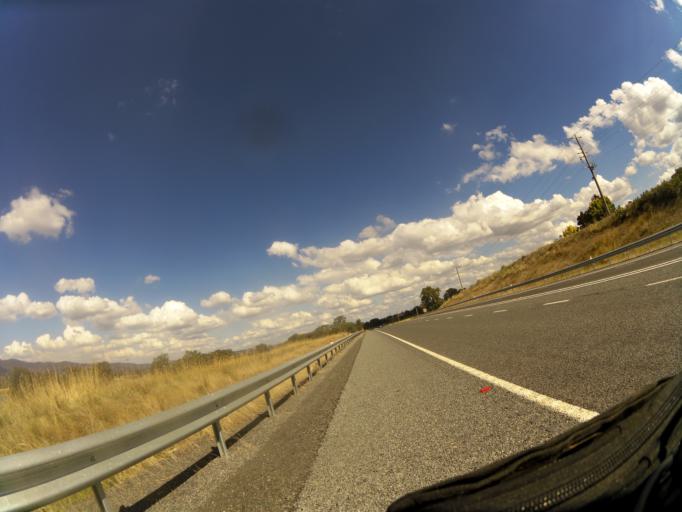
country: AU
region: Victoria
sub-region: Mansfield
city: Mansfield
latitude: -36.8893
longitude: 145.9955
